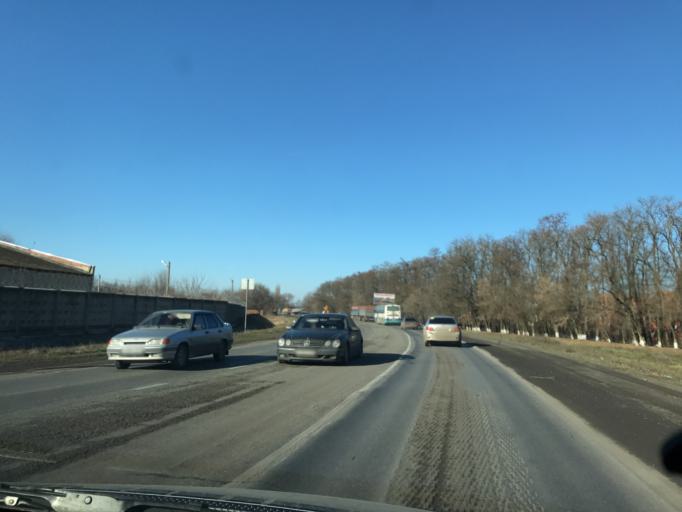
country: RU
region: Rostov
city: Kirovskaya
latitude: 46.9805
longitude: 40.0413
